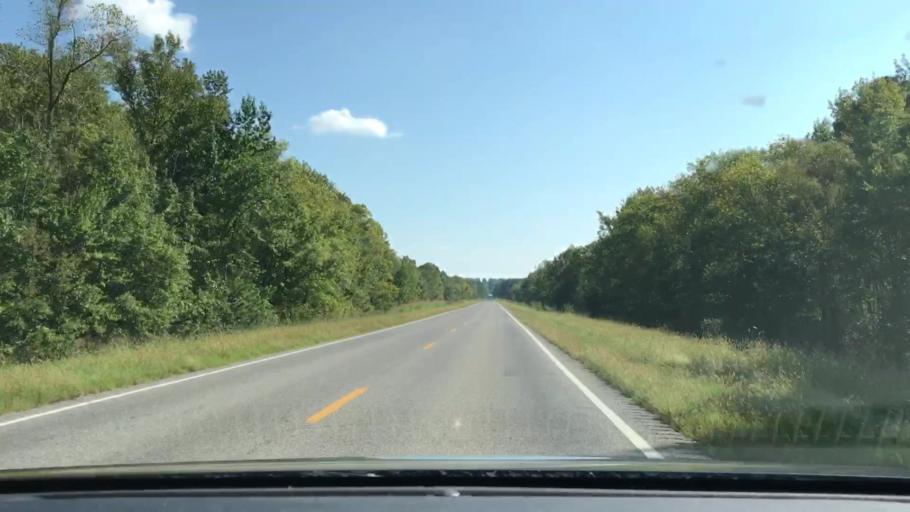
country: US
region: Kentucky
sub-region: Marshall County
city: Benton
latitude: 36.7648
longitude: -88.2403
